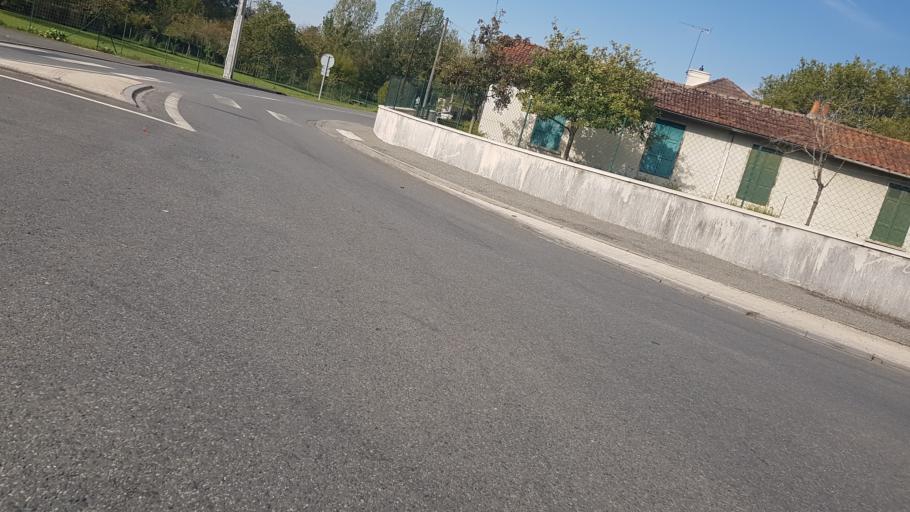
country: FR
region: Poitou-Charentes
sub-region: Departement de la Vienne
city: Chasseneuil-du-Poitou
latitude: 46.6312
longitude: 0.3692
